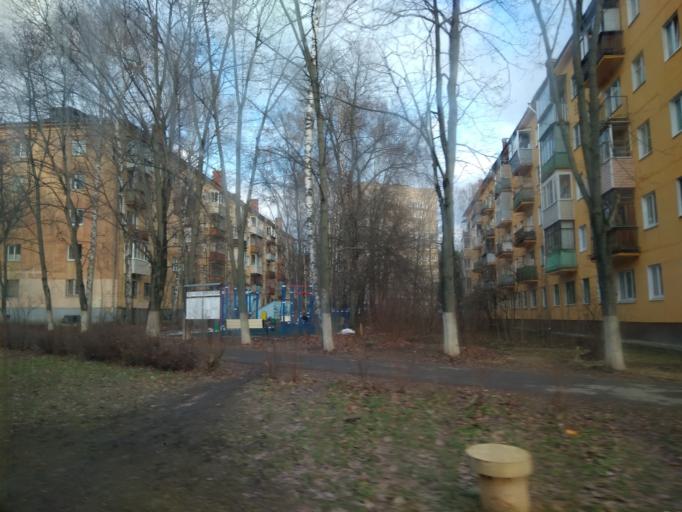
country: RU
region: Moskovskaya
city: Zhukovskiy
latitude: 55.5919
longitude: 38.1297
